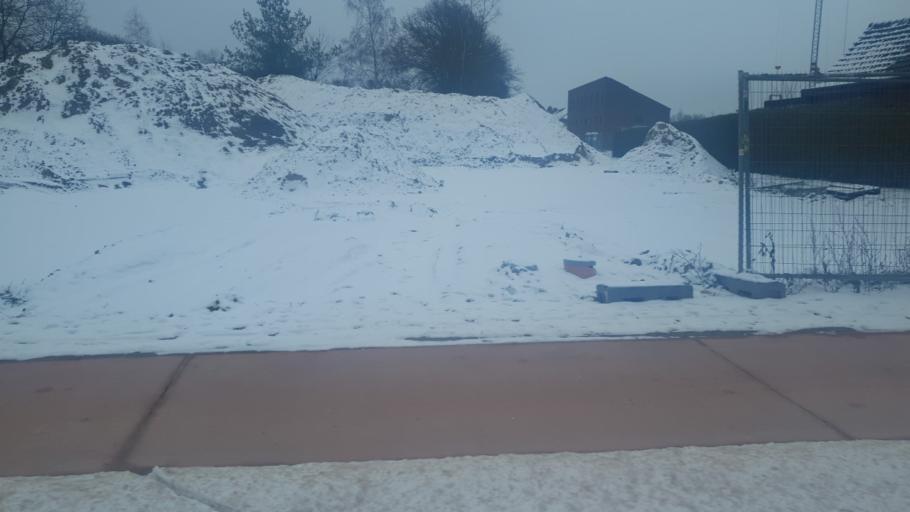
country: BE
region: Flanders
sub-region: Provincie Limburg
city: Overpelt
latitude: 51.2066
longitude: 5.4283
